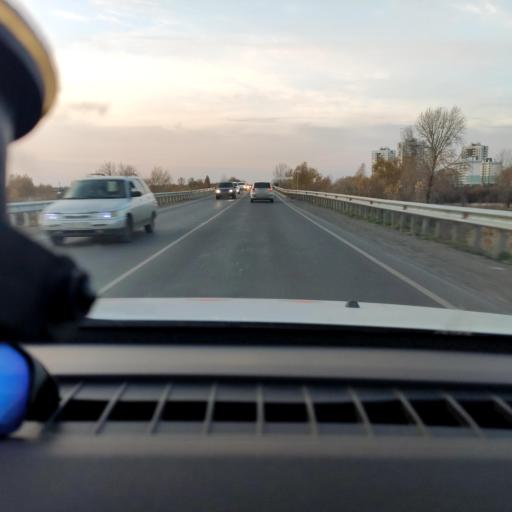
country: RU
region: Samara
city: Samara
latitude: 53.0999
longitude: 50.1421
